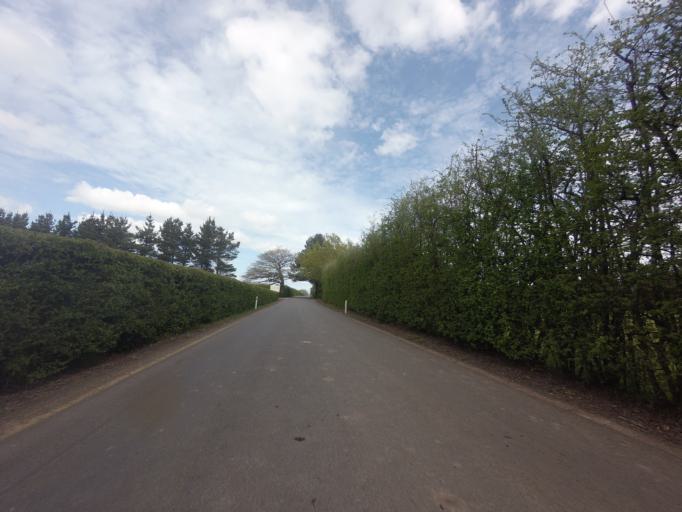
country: AU
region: Tasmania
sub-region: Northern Midlands
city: Longford
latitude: -41.6162
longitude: 147.1293
